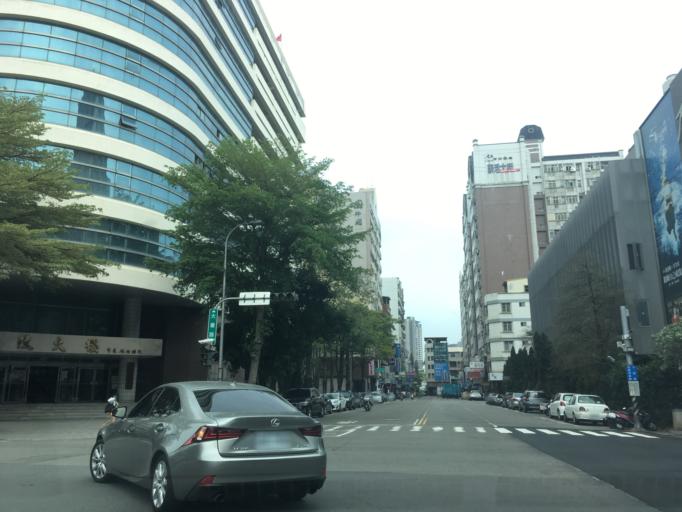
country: TW
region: Taiwan
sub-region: Taichung City
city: Taichung
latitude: 24.1536
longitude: 120.6530
